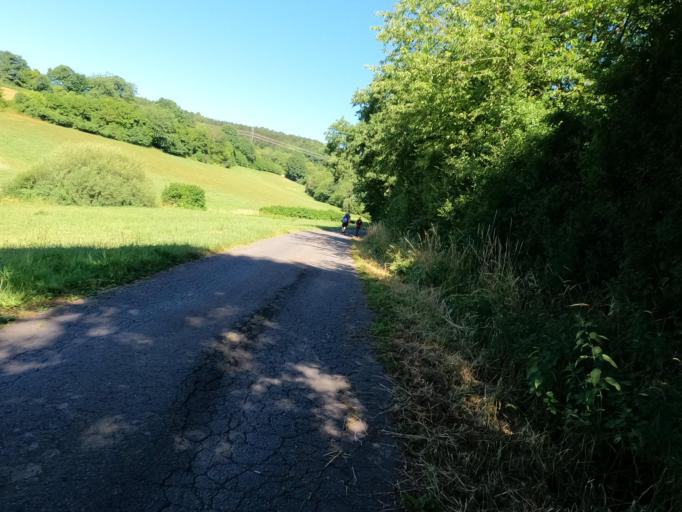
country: DE
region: Bavaria
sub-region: Regierungsbezirk Unterfranken
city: Zeitlofs
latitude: 50.3169
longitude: 9.6527
